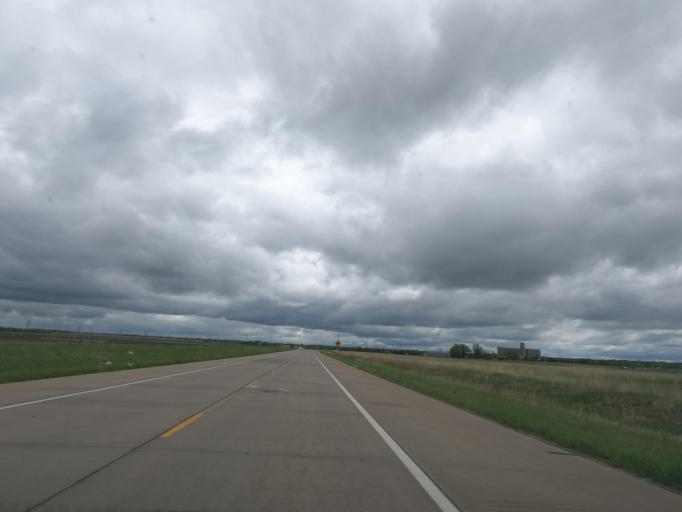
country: US
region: Kansas
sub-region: Wilson County
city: Fredonia
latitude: 37.5565
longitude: -95.8366
